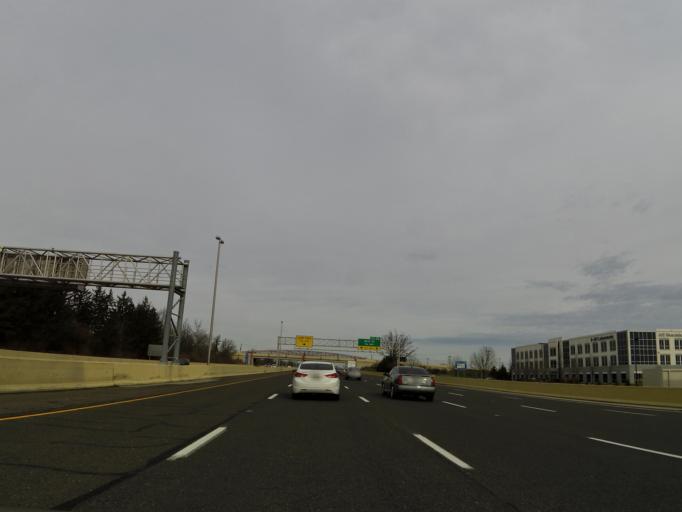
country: US
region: Indiana
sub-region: Boone County
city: Zionsville
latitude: 39.8930
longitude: -86.2695
